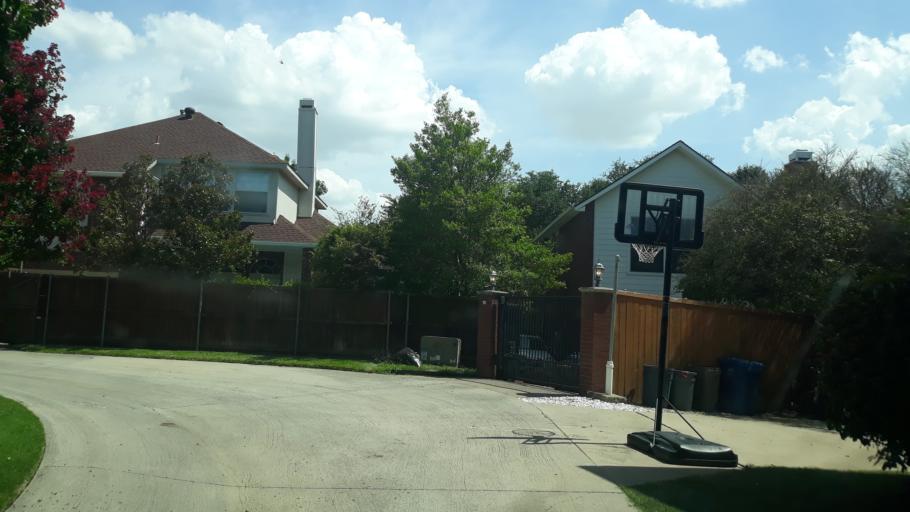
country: US
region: Texas
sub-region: Dallas County
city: Coppell
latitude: 32.9702
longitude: -97.0142
